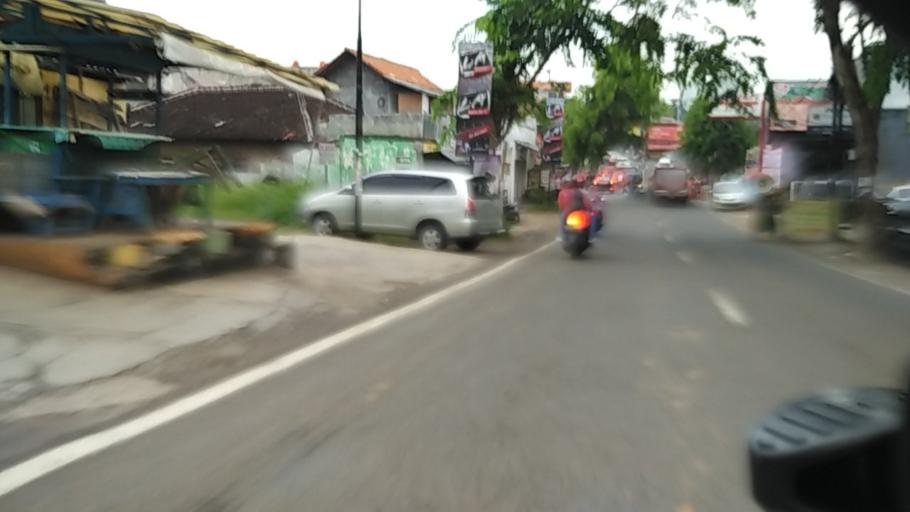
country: ID
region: Central Java
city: Semarang
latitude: -7.0549
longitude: 110.4301
